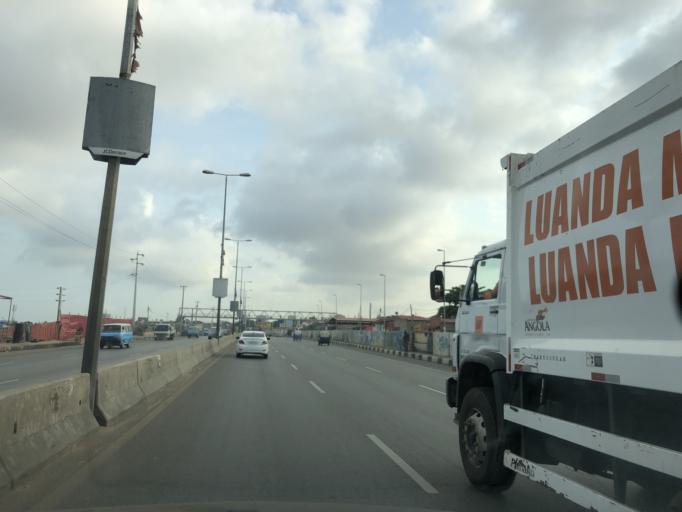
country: AO
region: Luanda
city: Luanda
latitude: -8.8544
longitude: 13.2194
